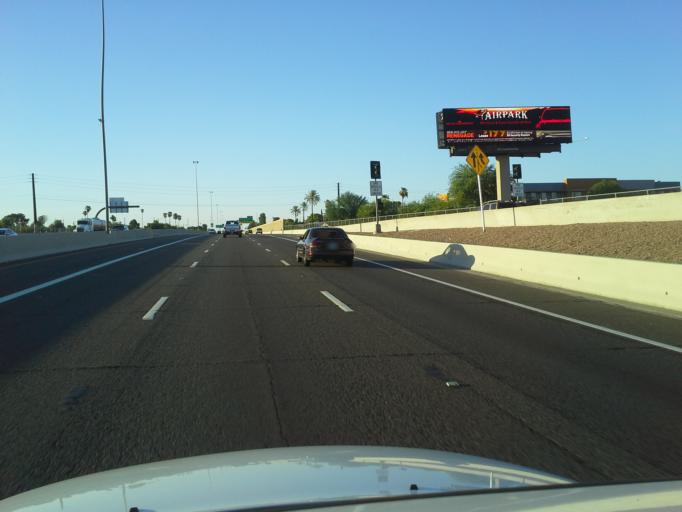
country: US
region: Arizona
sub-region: Maricopa County
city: Phoenix
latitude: 33.5116
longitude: -112.1123
